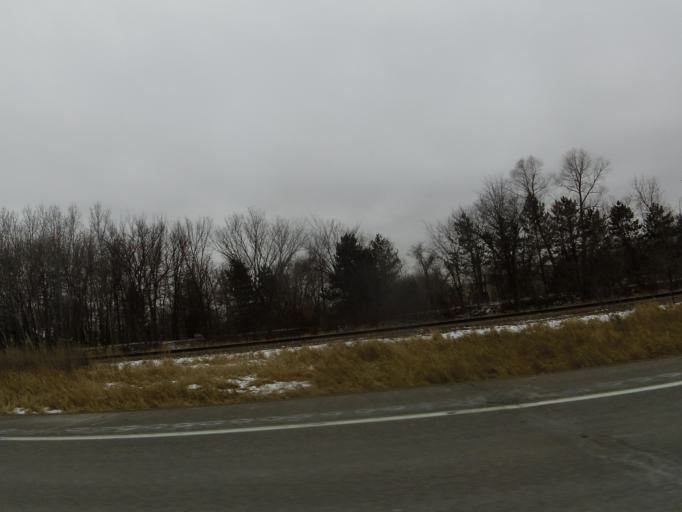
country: US
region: Minnesota
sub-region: Hennepin County
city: Maple Plain
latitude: 45.0005
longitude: -93.6370
